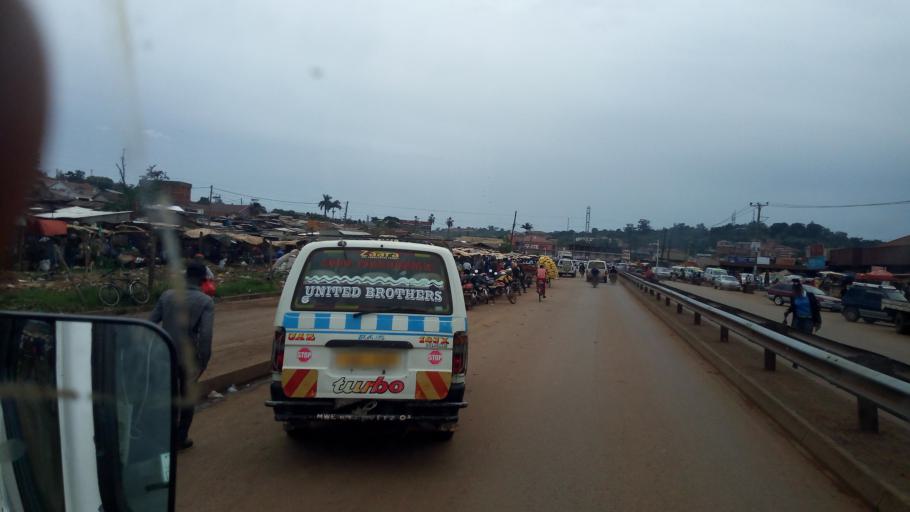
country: UG
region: Central Region
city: Kampala Central Division
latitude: 0.3509
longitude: 32.5714
